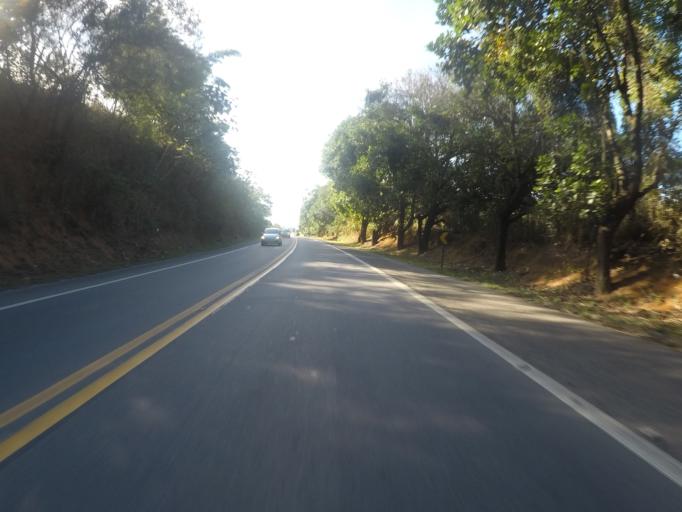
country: BR
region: Espirito Santo
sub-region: Fundao
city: Fundao
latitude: -19.9217
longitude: -40.4056
